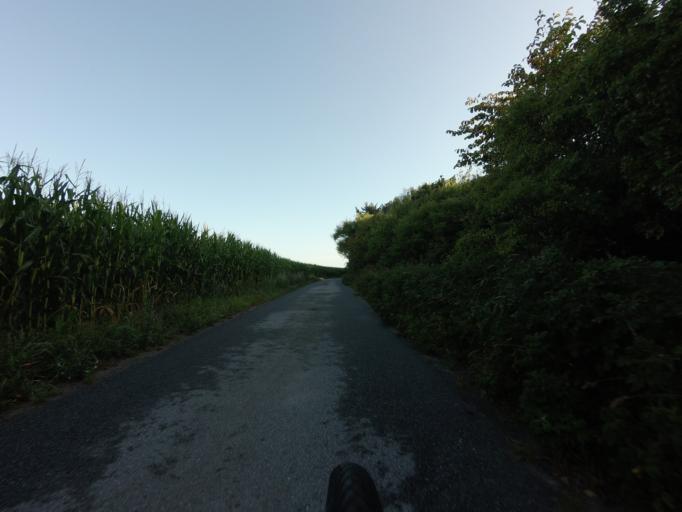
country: DK
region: North Denmark
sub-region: Hjorring Kommune
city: Vra
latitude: 57.3660
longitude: 9.8649
